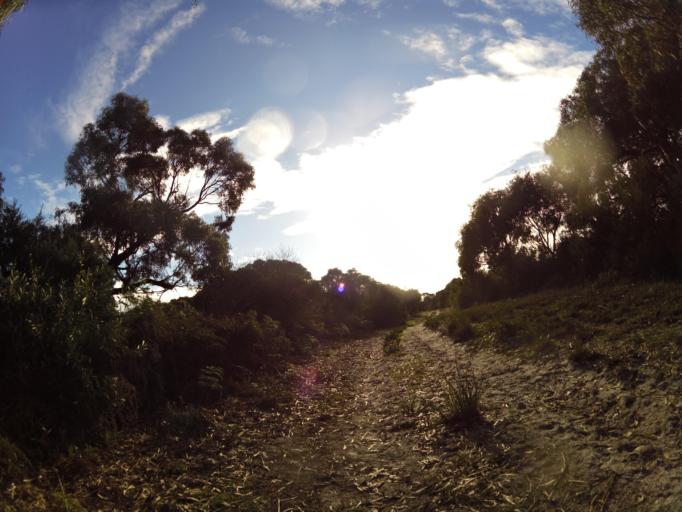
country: AU
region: Victoria
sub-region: Bass Coast
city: North Wonthaggi
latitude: -38.6338
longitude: 145.5683
